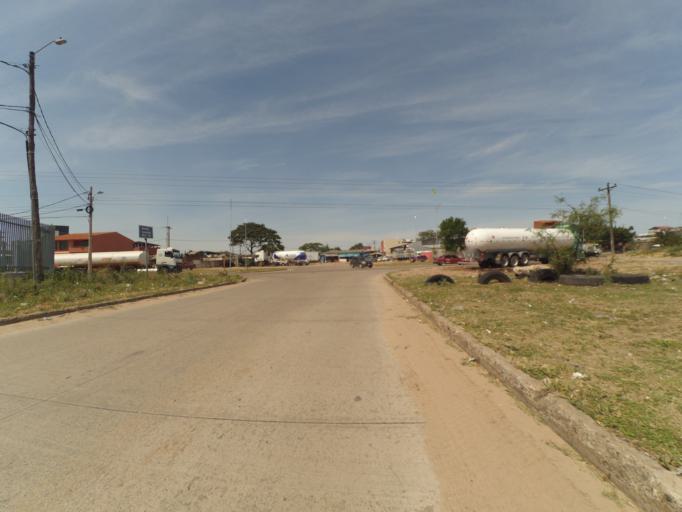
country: BO
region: Santa Cruz
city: Santa Cruz de la Sierra
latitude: -17.8150
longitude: -63.2154
